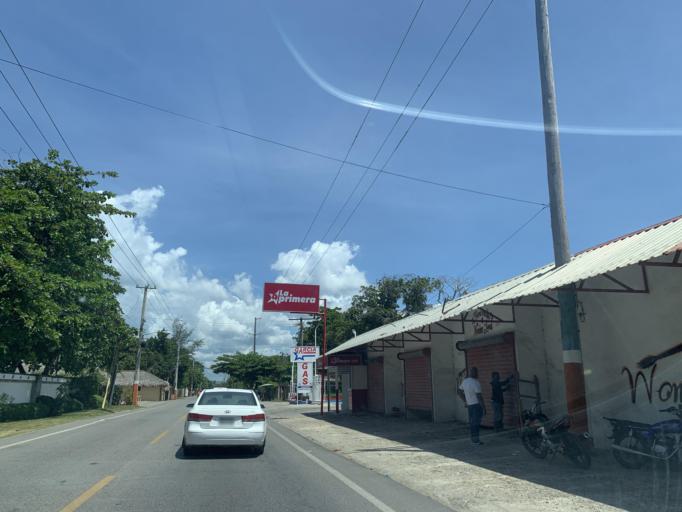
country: DO
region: Puerto Plata
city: Cabarete
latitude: 19.7439
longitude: -70.3941
